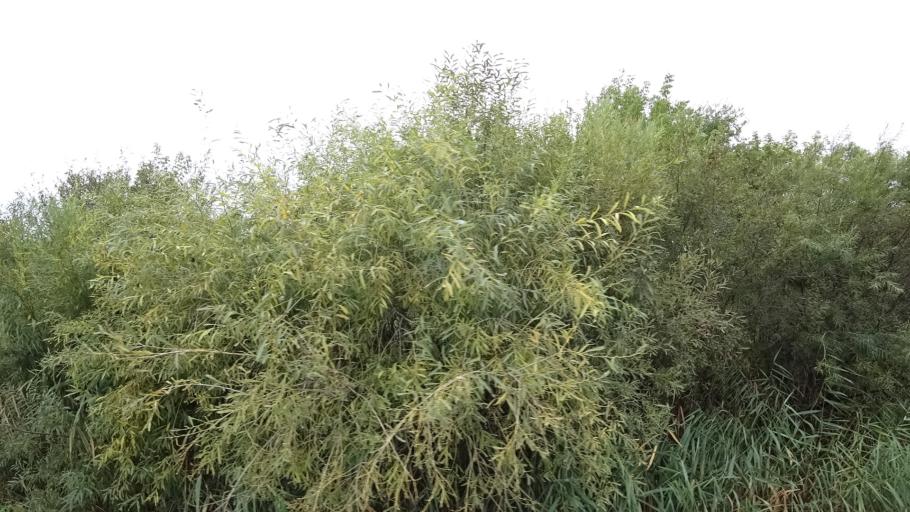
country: RU
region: Primorskiy
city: Monastyrishche
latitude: 44.1882
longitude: 132.4829
